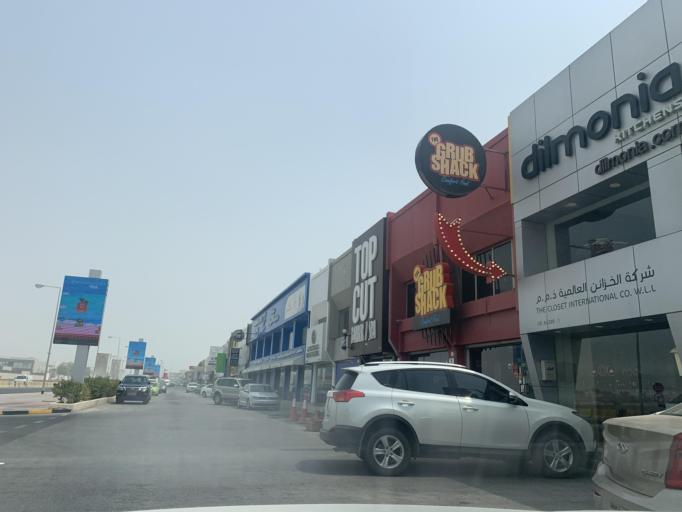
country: BH
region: Central Governorate
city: Madinat Hamad
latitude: 26.1682
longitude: 50.4664
